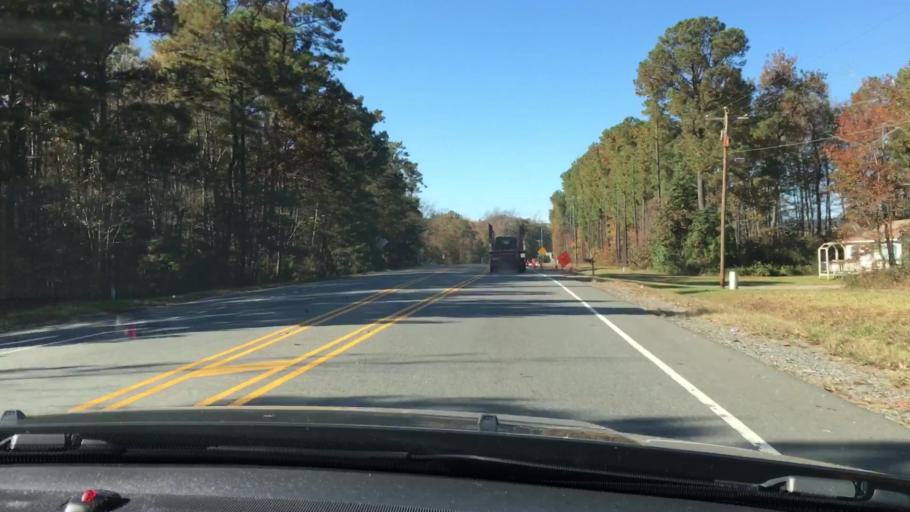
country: US
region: Virginia
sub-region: King William County
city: Central Garage
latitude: 37.7466
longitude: -77.1357
